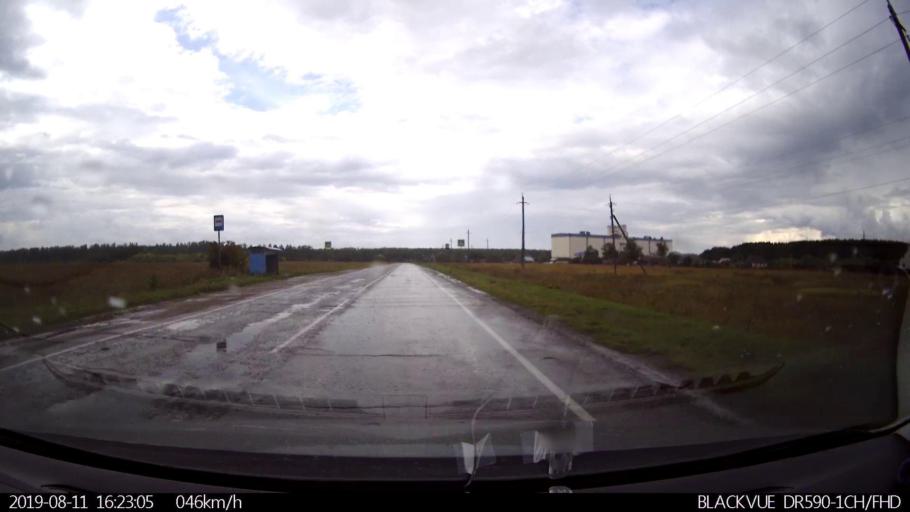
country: RU
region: Ulyanovsk
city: Mayna
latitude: 54.0927
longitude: 47.5900
